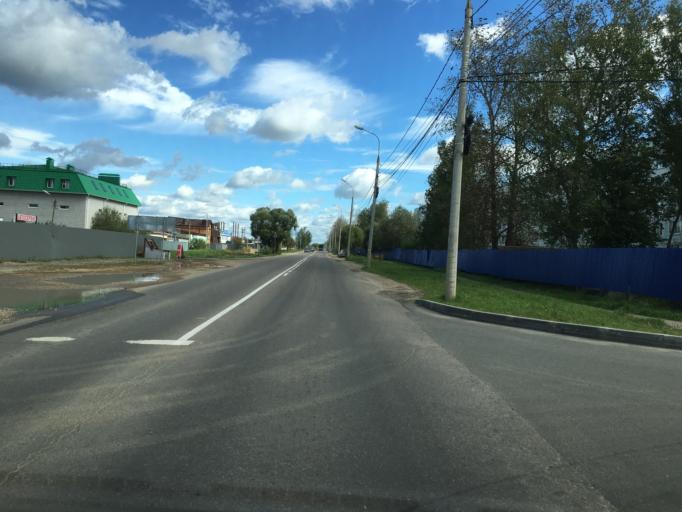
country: RU
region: Kaluga
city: Kaluga
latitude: 54.5521
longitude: 36.3456
